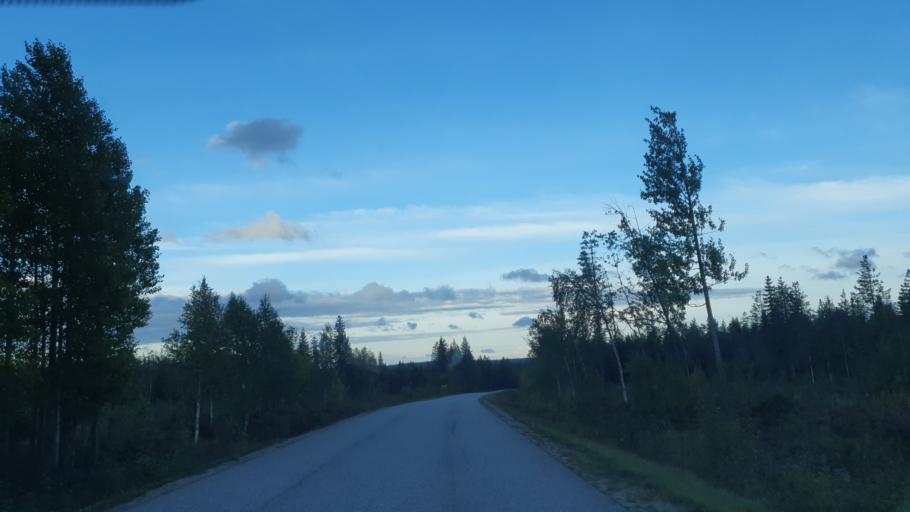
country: FI
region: Kainuu
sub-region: Kehys-Kainuu
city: Kuhmo
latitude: 64.4179
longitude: 29.9008
